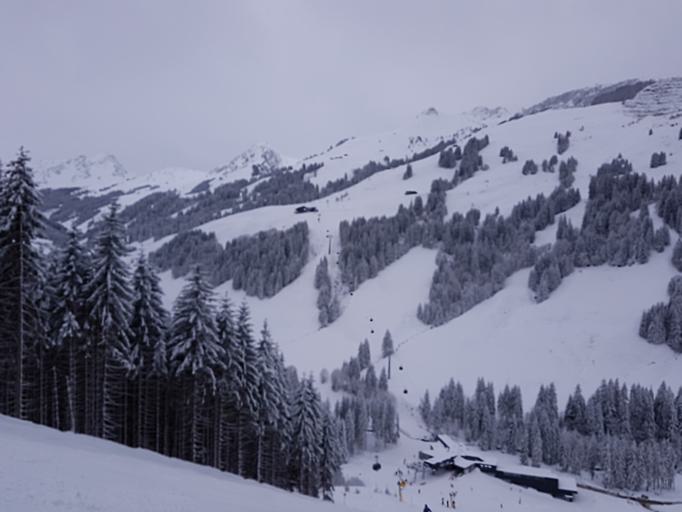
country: AT
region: Salzburg
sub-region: Politischer Bezirk Zell am See
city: Saalbach
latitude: 47.4164
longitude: 12.5819
